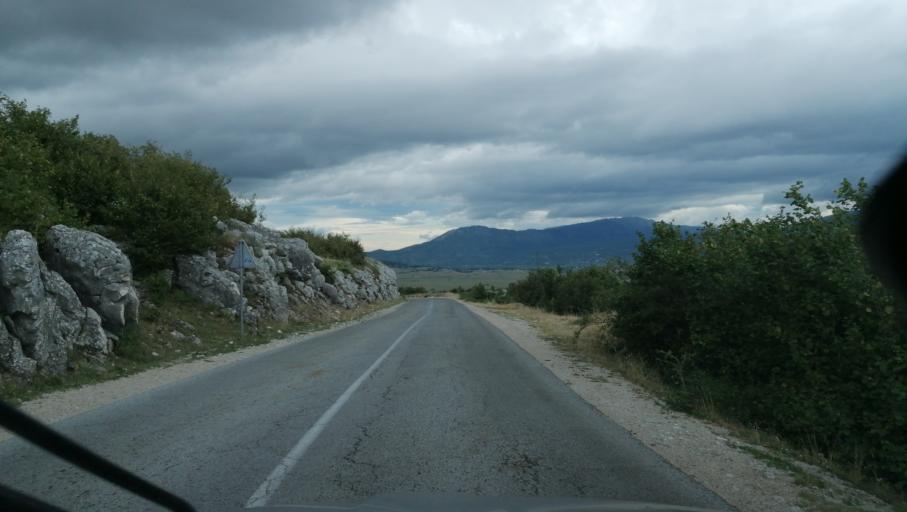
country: BA
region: Republika Srpska
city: Gacko
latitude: 43.1597
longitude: 18.5677
